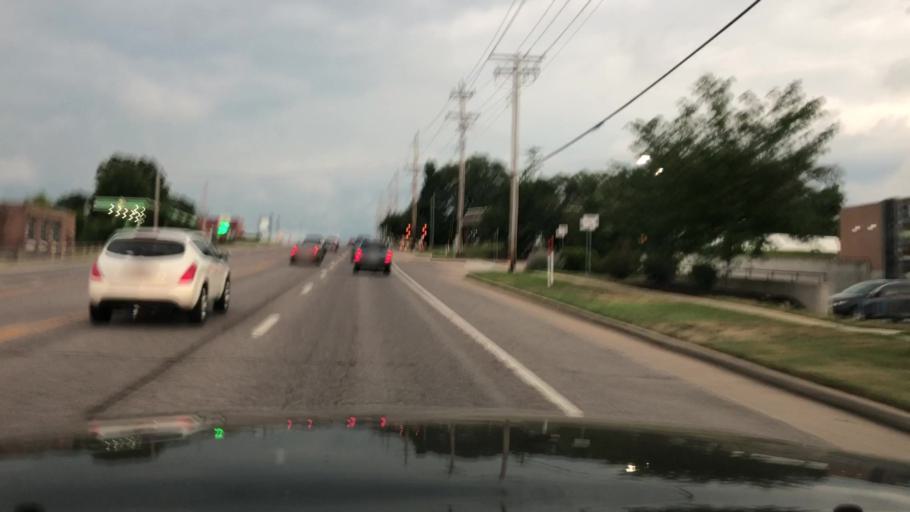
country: US
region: Missouri
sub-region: Saint Louis County
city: Bridgeton
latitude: 38.7459
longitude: -90.4185
